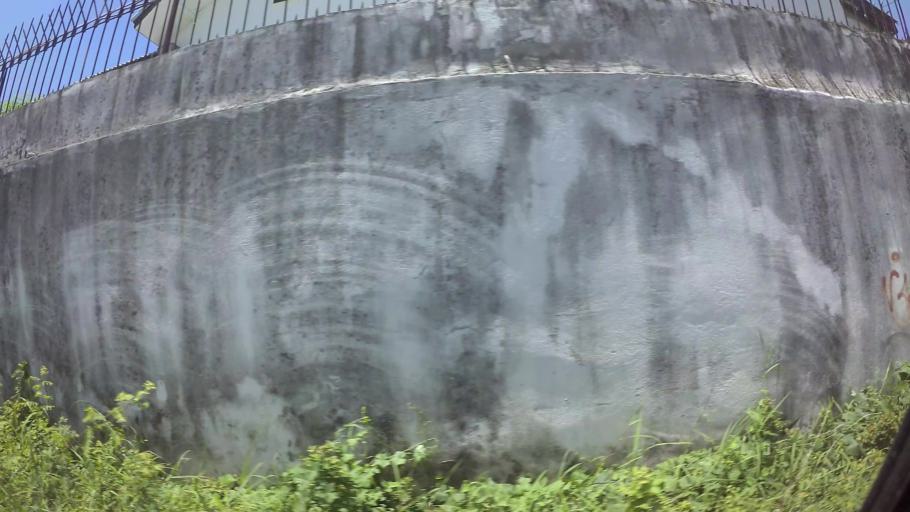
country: TH
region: Chon Buri
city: Phatthaya
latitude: 12.9259
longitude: 100.8957
